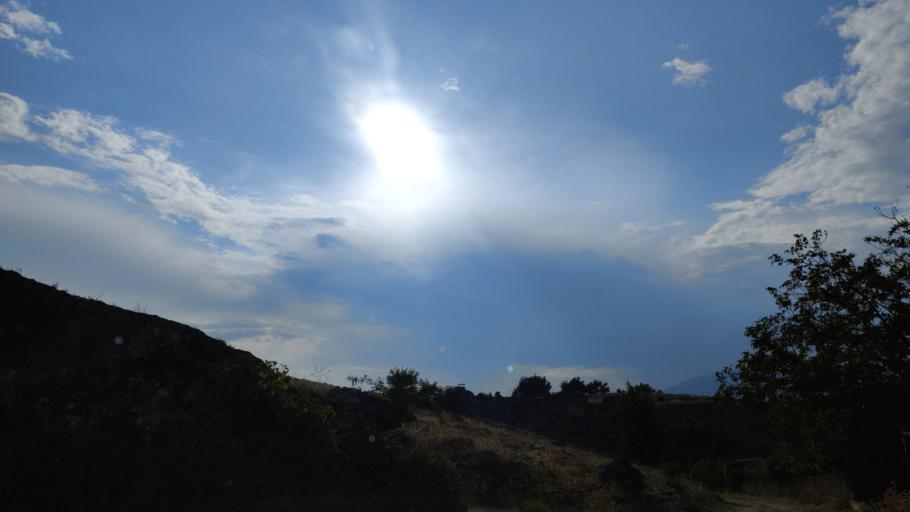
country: GR
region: Central Macedonia
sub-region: Nomos Serron
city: Sidirokastro
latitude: 41.2387
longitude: 23.3998
